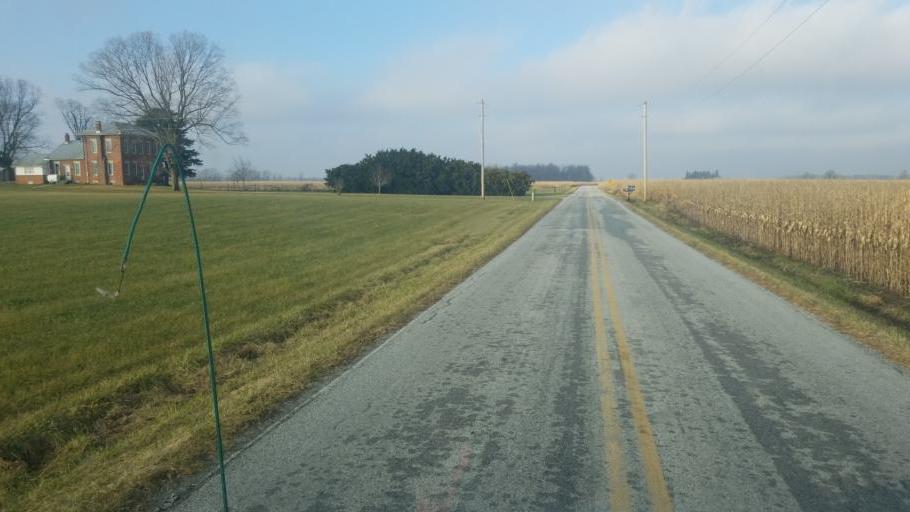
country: US
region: Ohio
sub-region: Hardin County
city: Kenton
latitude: 40.6887
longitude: -83.5951
